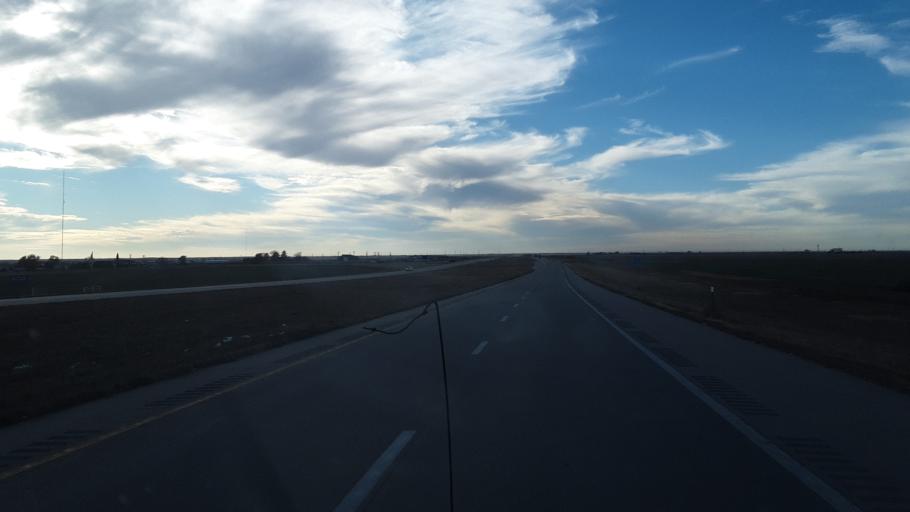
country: US
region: Kansas
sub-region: Finney County
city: Garden City
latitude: 38.0034
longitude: -100.8953
